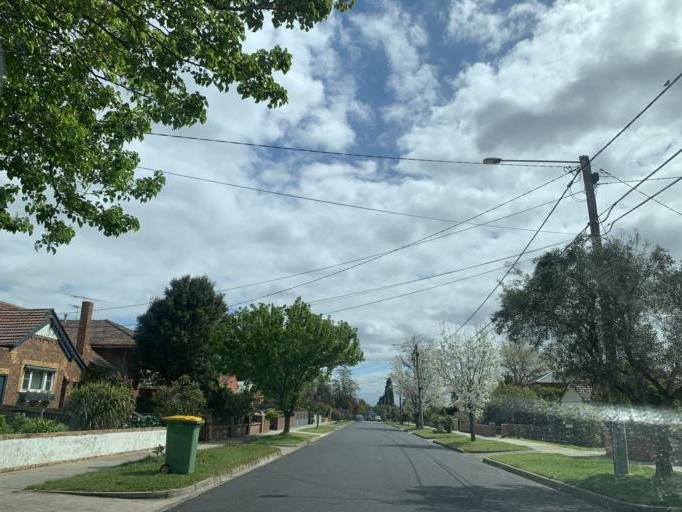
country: AU
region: Victoria
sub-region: Darebin
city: Reservoir
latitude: -37.7324
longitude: 144.9894
